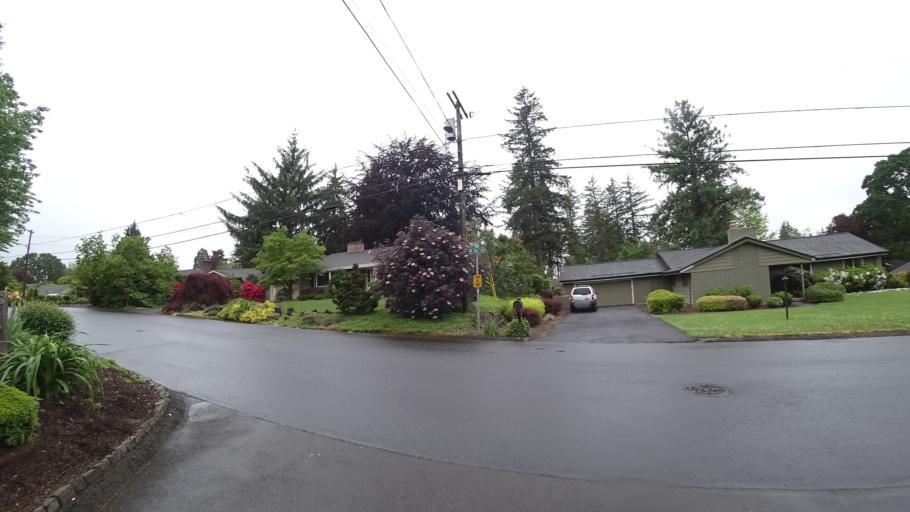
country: US
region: Oregon
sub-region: Washington County
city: Raleigh Hills
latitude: 45.4755
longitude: -122.7693
